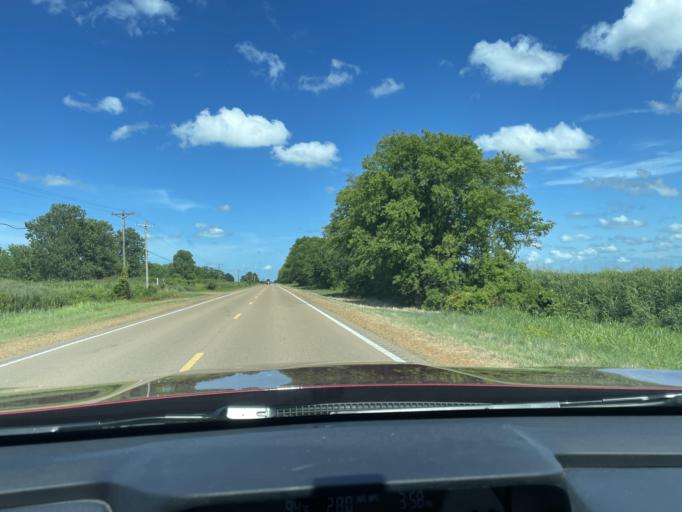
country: US
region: Mississippi
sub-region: Humphreys County
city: Belzoni
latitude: 33.1837
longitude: -90.5859
